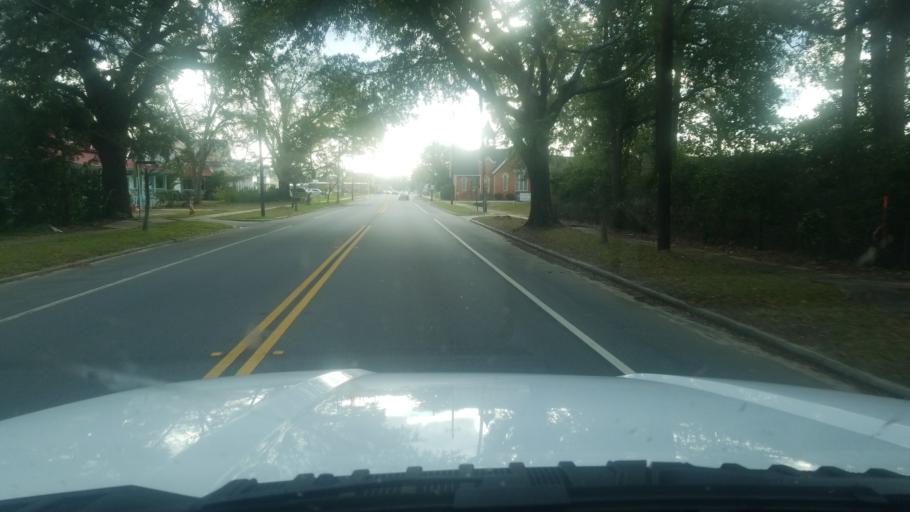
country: US
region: Georgia
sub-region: Tattnall County
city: Reidsville
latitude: 32.0891
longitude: -82.1157
